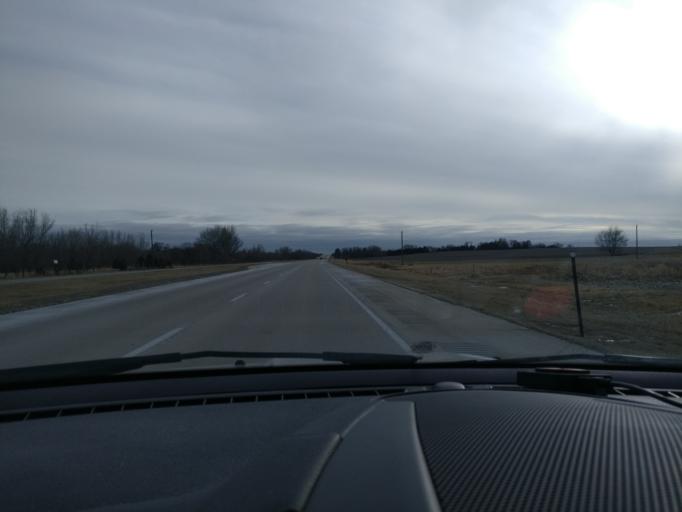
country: US
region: Nebraska
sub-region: Lancaster County
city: Waverly
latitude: 41.0239
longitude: -96.6406
